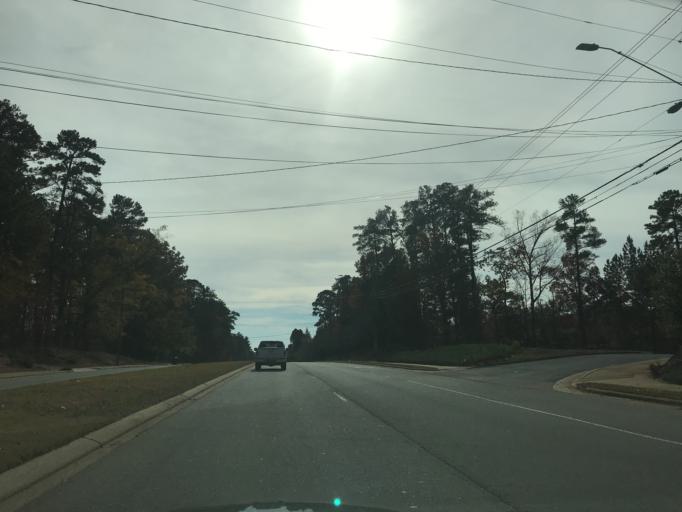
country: US
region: North Carolina
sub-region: Wake County
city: West Raleigh
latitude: 35.8559
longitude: -78.6806
